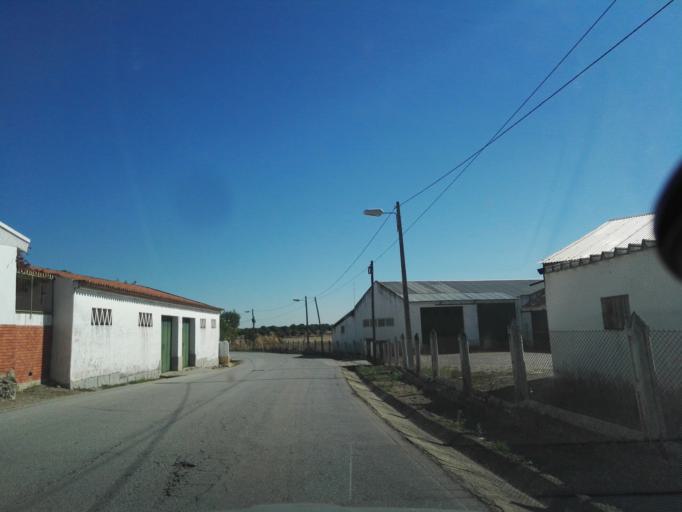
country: PT
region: Portalegre
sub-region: Elvas
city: Elvas
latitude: 38.8894
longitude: -7.1397
